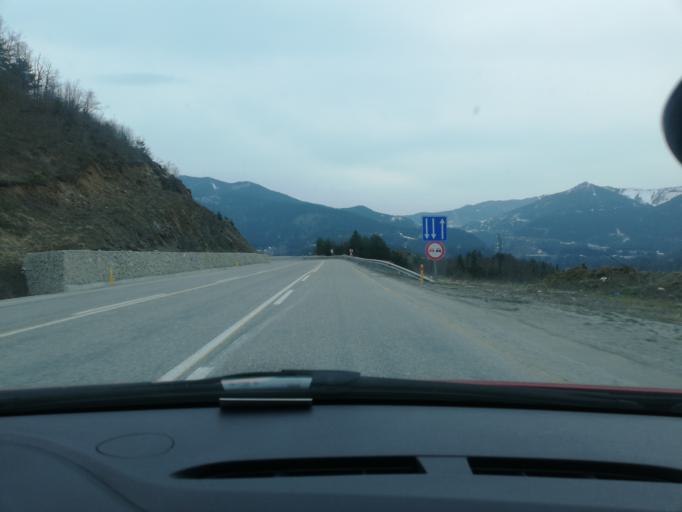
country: TR
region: Kastamonu
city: Kure
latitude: 41.8505
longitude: 33.7137
